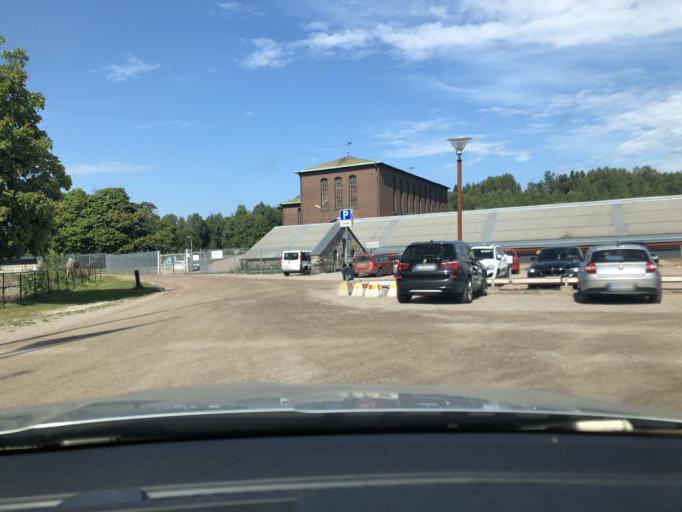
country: SE
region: Dalarna
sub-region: Avesta Kommun
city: Avesta
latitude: 60.1491
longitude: 16.1702
